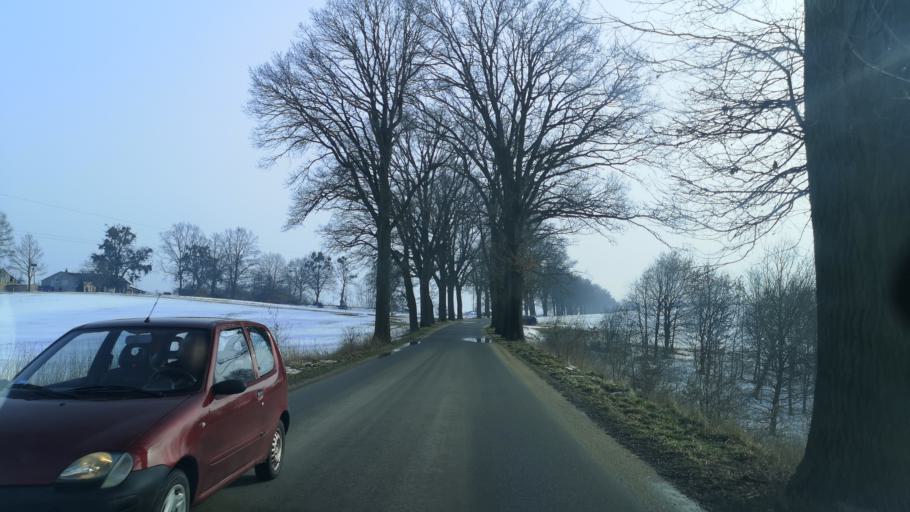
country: PL
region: Warmian-Masurian Voivodeship
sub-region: Powiat nowomiejski
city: Biskupiec
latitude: 53.5202
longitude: 19.3469
